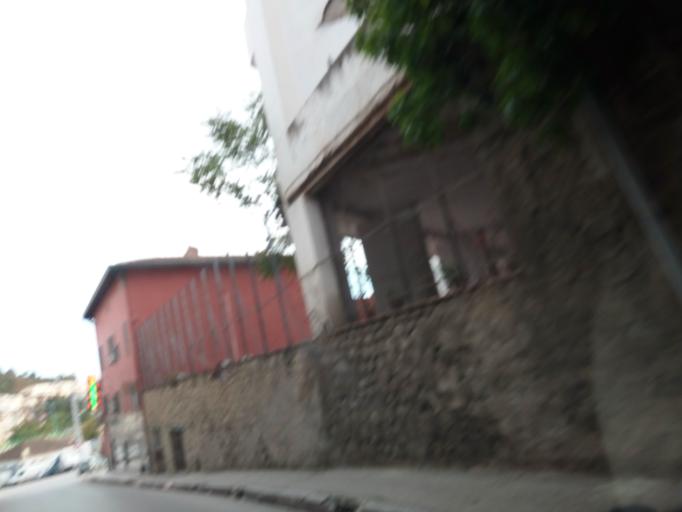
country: DZ
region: Constantine
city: Constantine
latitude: 36.3707
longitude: 6.6196
